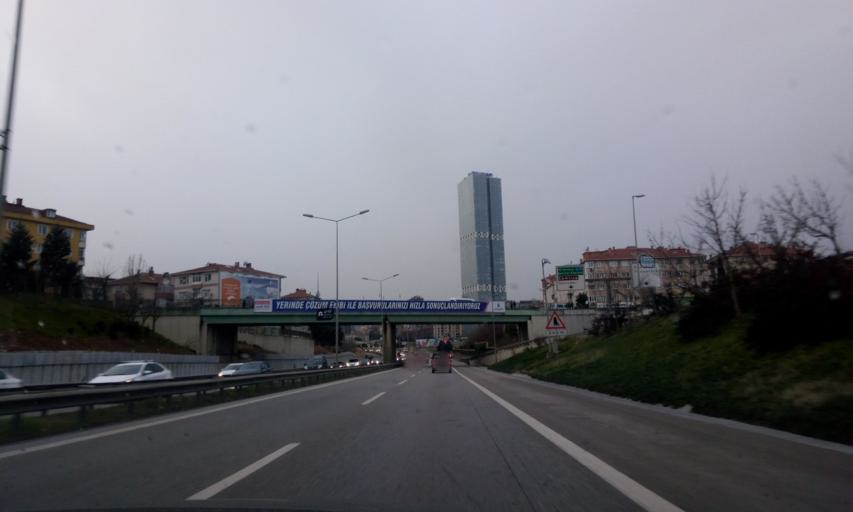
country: TR
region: Istanbul
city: Umraniye
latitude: 41.0307
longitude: 29.0977
